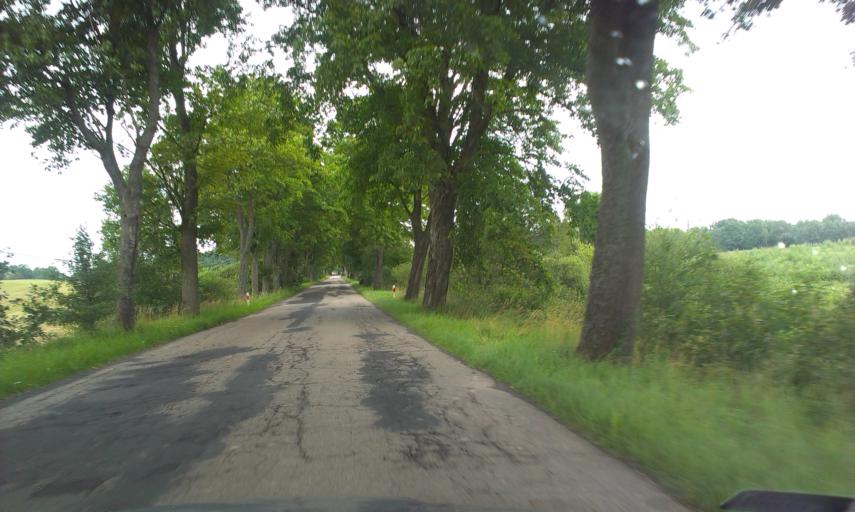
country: PL
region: West Pomeranian Voivodeship
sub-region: Powiat szczecinecki
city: Barwice
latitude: 53.6978
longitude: 16.3495
